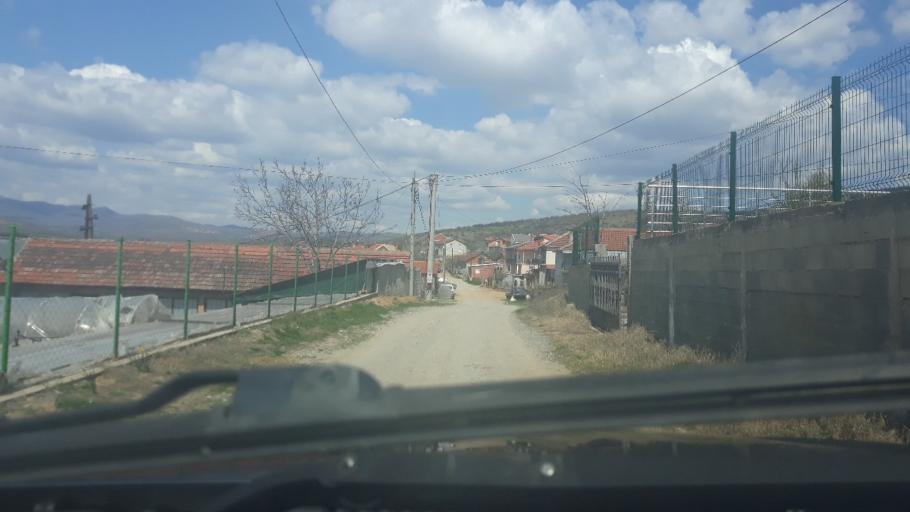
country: MK
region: Caska
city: Caska
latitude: 41.6491
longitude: 21.6936
